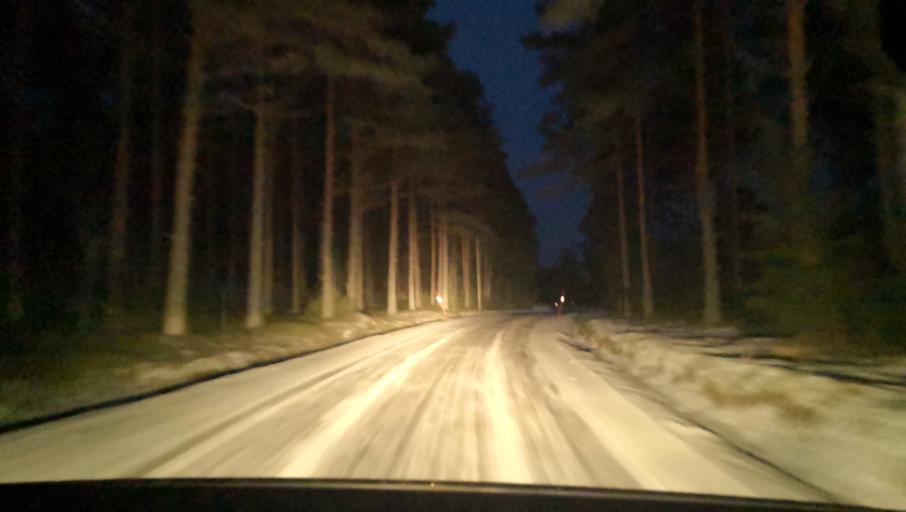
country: SE
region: Uppsala
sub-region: Heby Kommun
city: Tarnsjo
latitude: 60.2766
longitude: 16.8002
